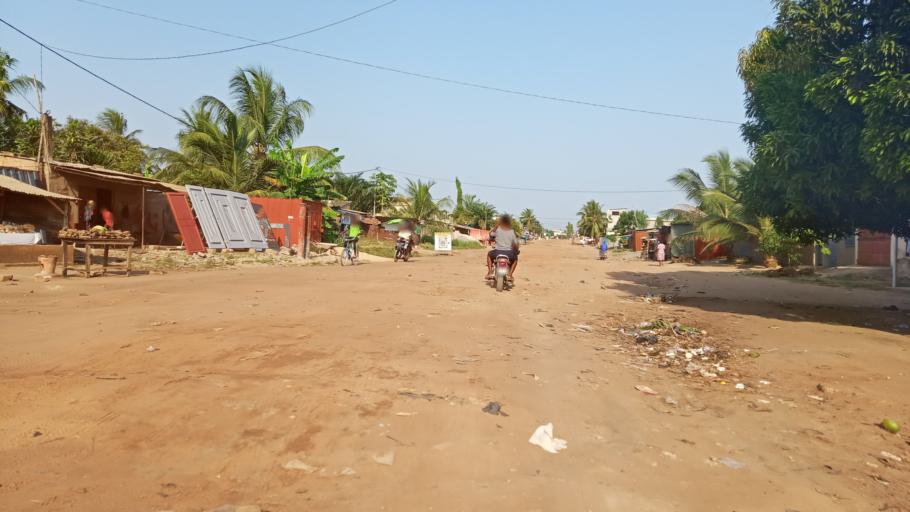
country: TG
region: Maritime
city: Lome
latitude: 6.1793
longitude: 1.1508
